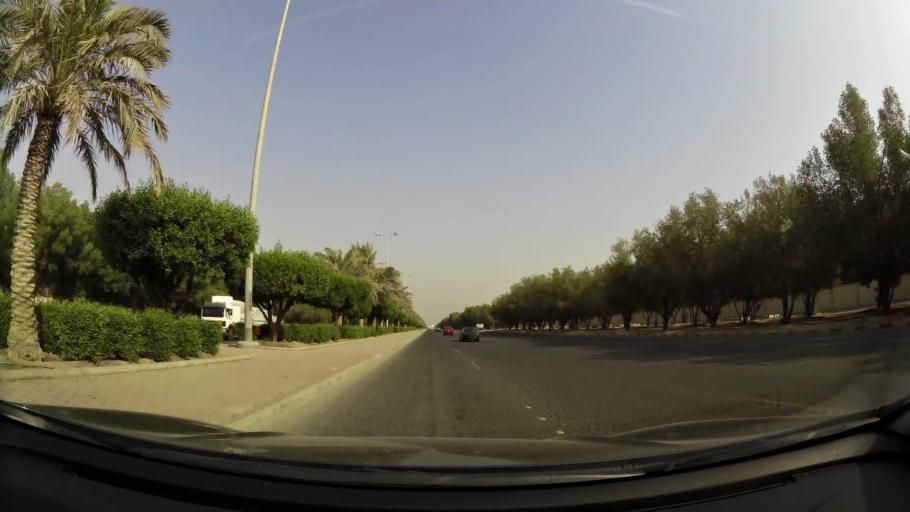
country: KW
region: Al Asimah
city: Ar Rabiyah
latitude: 29.2995
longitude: 47.8322
